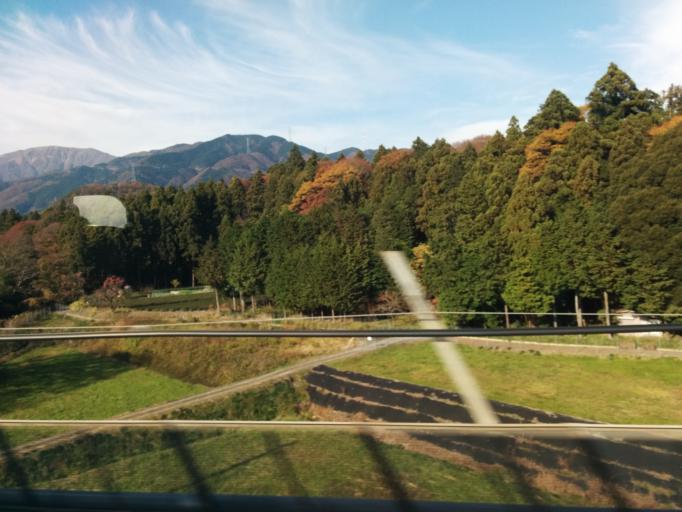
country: JP
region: Gifu
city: Tarui
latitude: 35.3563
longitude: 136.4597
